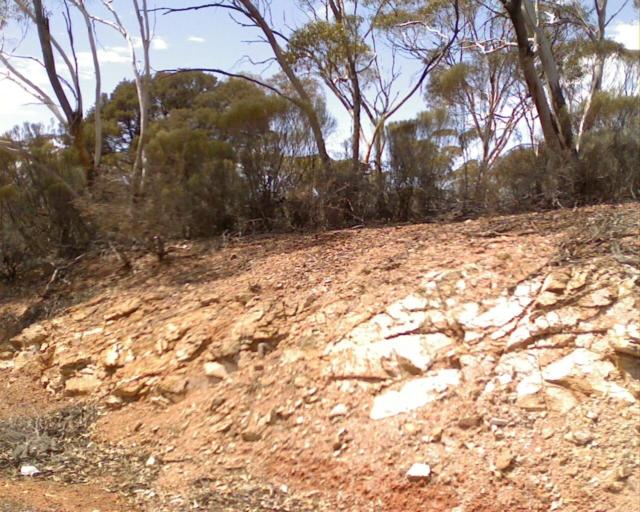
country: AU
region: Western Australia
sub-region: Kalgoorlie/Boulder
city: Stoneville
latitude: -31.2068
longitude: 121.6657
